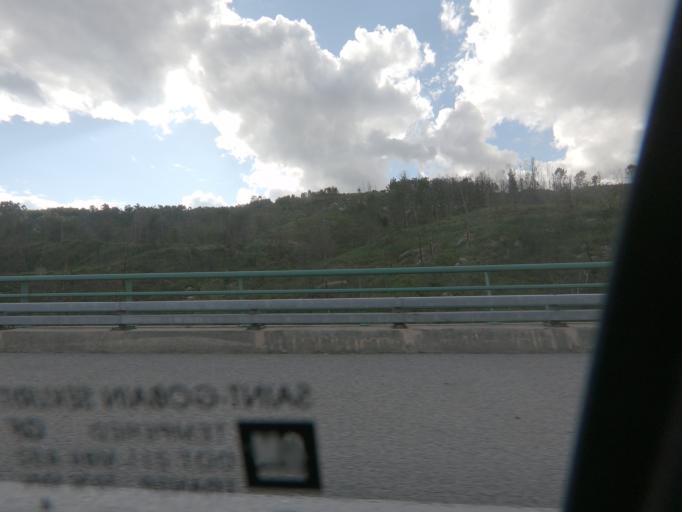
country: PT
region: Porto
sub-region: Amarante
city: Amarante
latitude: 41.2396
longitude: -8.1195
